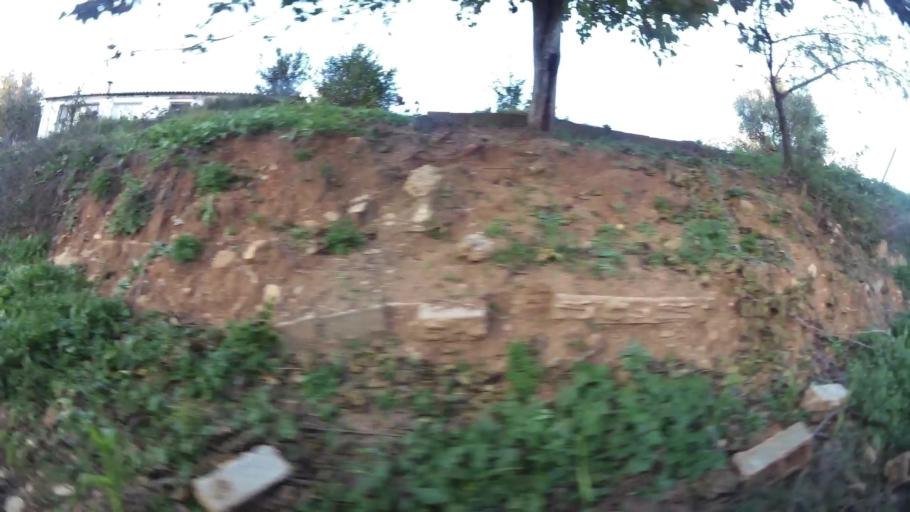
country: GR
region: Attica
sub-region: Nomarchia Anatolikis Attikis
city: Kryoneri
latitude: 38.1465
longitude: 23.8336
